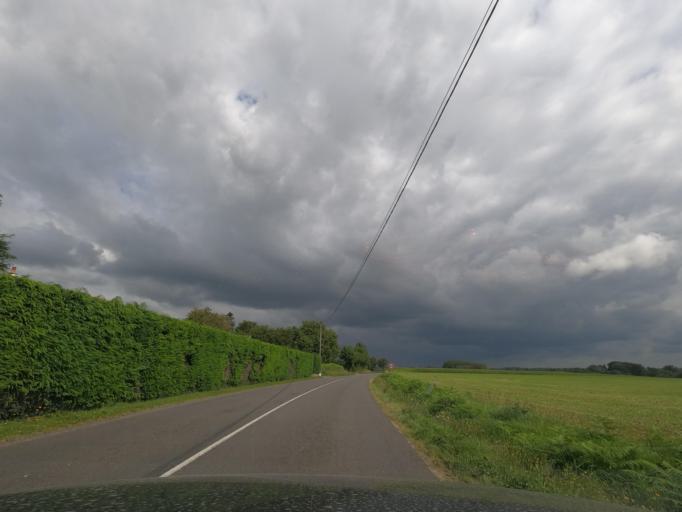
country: FR
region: Lower Normandy
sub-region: Departement de l'Orne
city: Briouze
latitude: 48.6917
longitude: -0.4331
